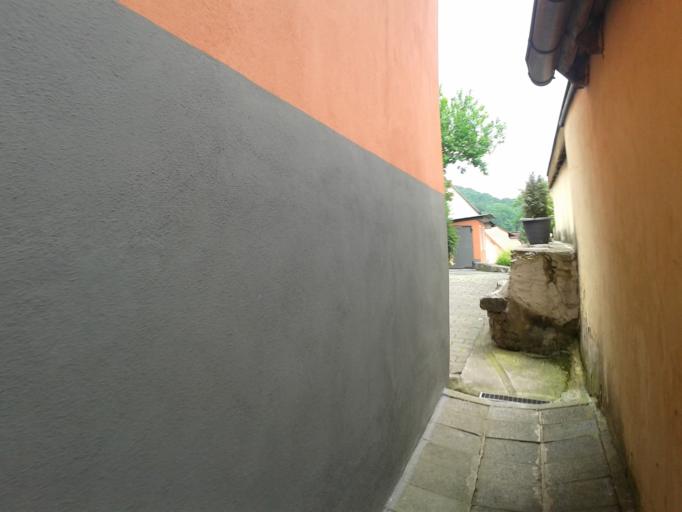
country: DE
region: Bavaria
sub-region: Upper Franconia
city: Grafenberg
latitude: 49.6441
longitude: 11.2487
